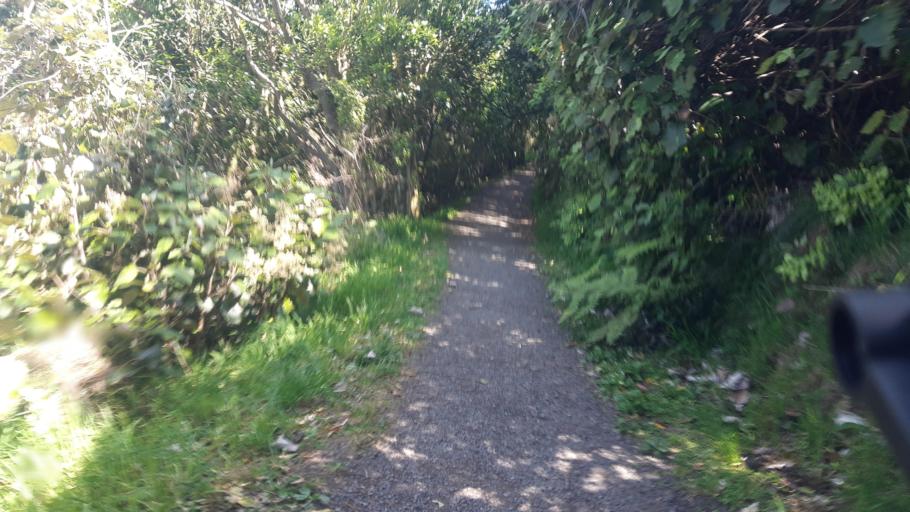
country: NZ
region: Marlborough
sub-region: Marlborough District
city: Picton
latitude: -41.2693
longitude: 174.0333
